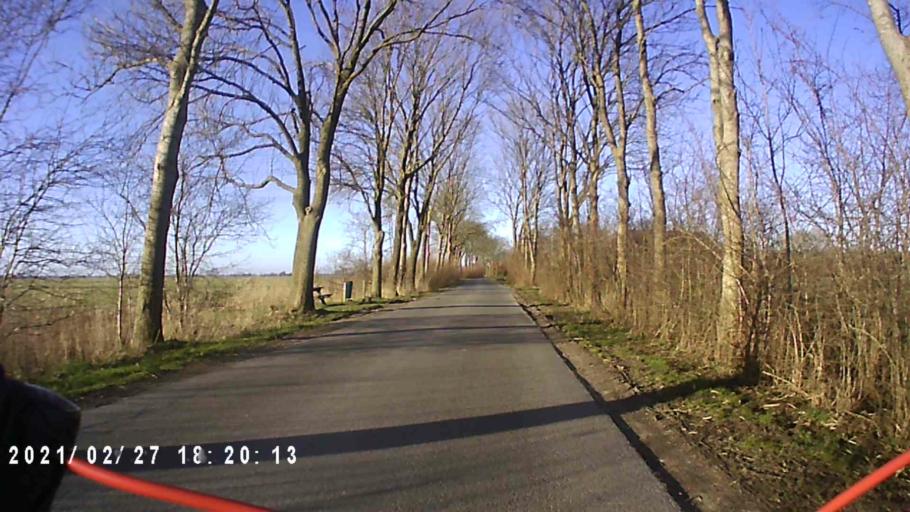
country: NL
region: Groningen
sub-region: Gemeente Bedum
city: Bedum
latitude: 53.3059
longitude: 6.5747
